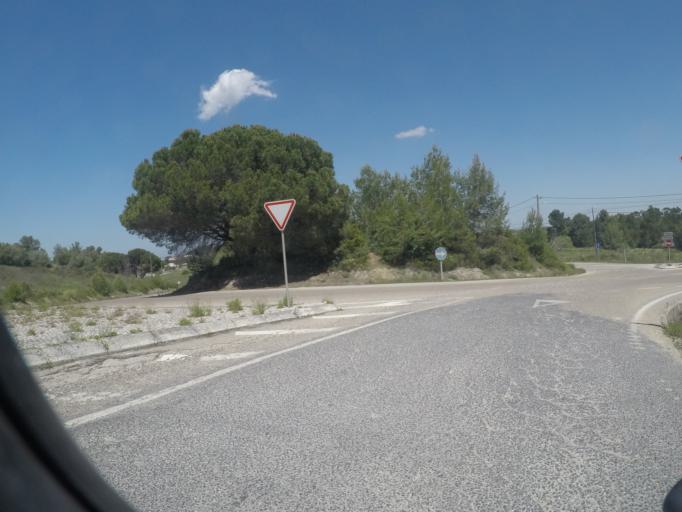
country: PT
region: Setubal
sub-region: Sesimbra
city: Sesimbra
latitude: 38.4634
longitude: -9.0786
